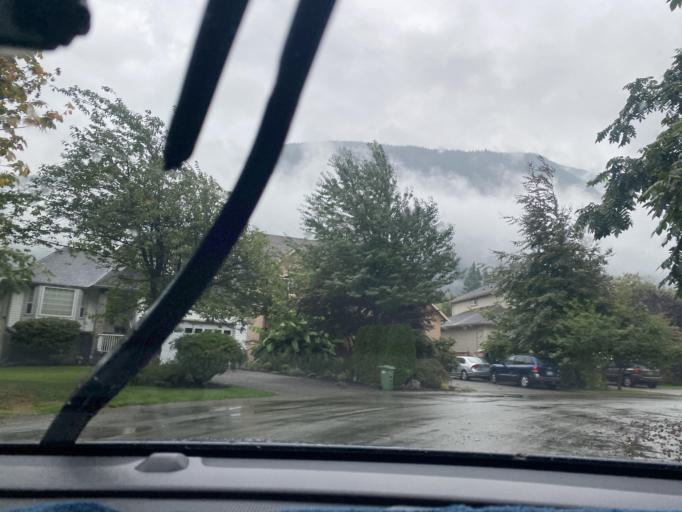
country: CA
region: British Columbia
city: Agassiz
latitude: 49.3015
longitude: -121.7809
